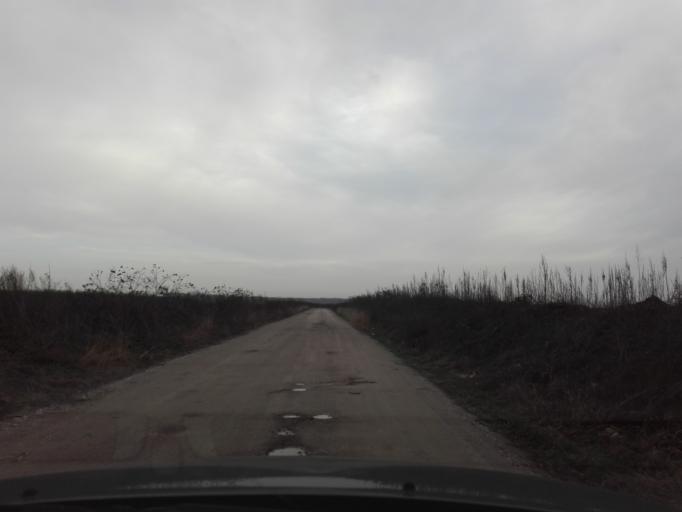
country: AT
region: Upper Austria
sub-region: Politischer Bezirk Linz-Land
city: Horsching
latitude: 48.2186
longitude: 14.1542
